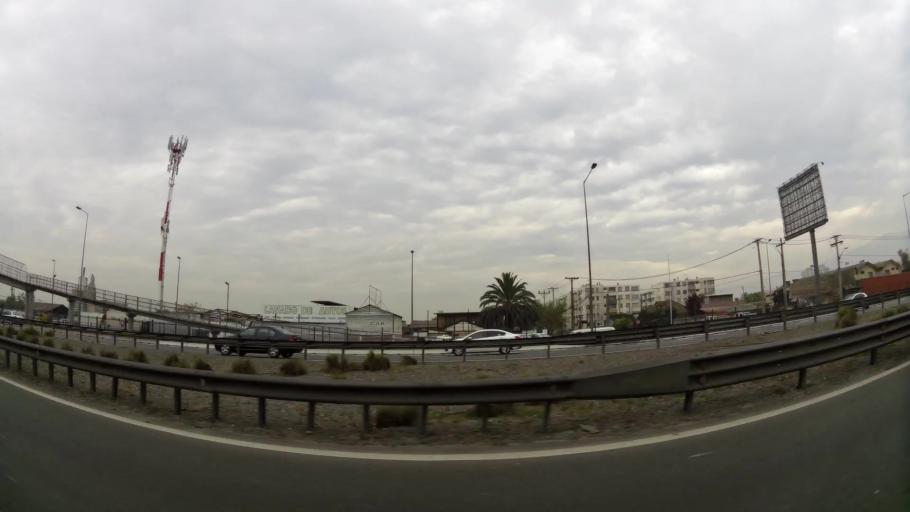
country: CL
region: Santiago Metropolitan
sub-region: Provincia de Santiago
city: La Pintana
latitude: -33.5356
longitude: -70.6703
